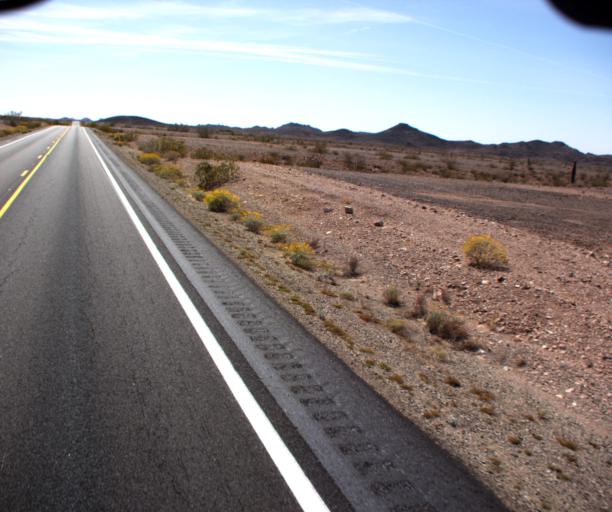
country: US
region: Arizona
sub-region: Yuma County
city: Wellton
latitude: 33.1263
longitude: -114.2904
